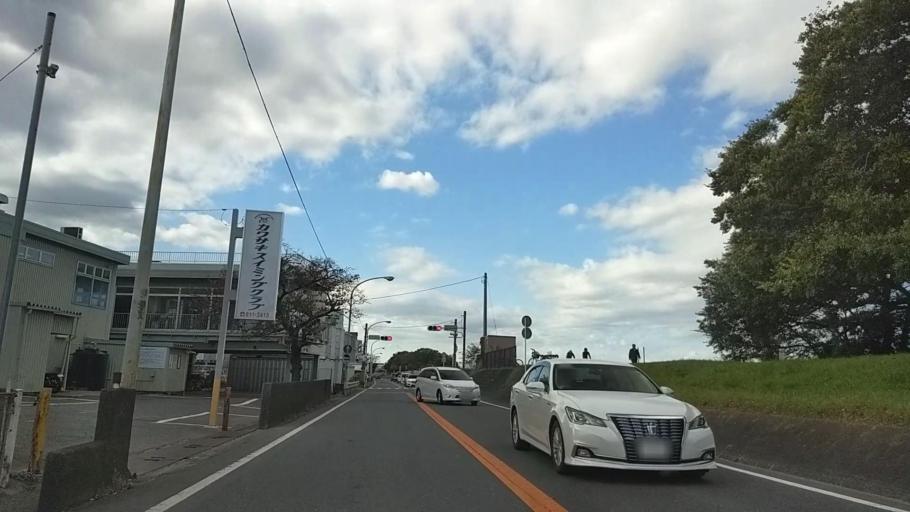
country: JP
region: Tokyo
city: Chofugaoka
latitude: 35.6151
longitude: 139.6014
